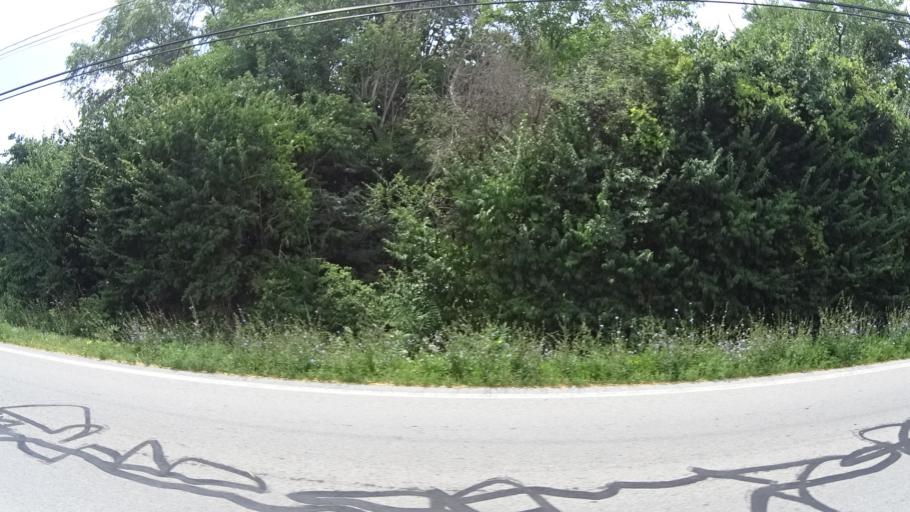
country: US
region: Ohio
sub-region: Erie County
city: Sandusky
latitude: 41.4056
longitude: -82.7713
